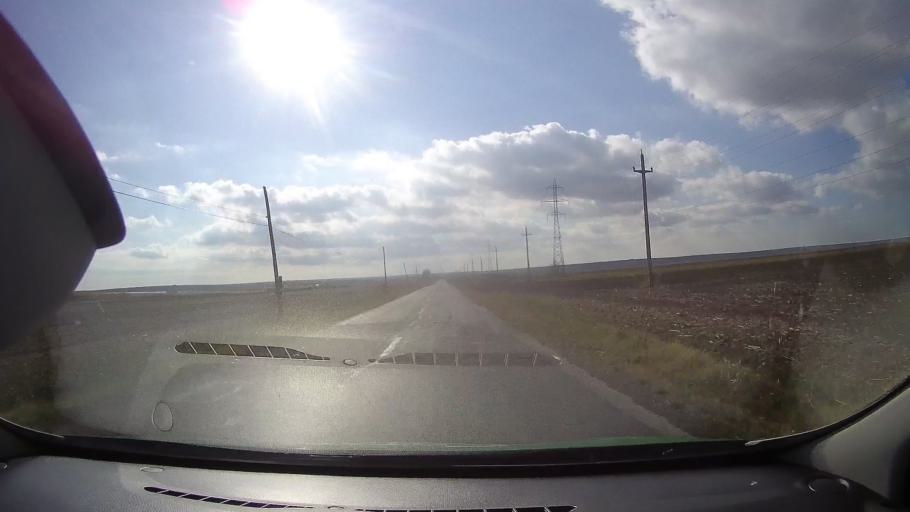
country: RO
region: Constanta
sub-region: Comuna Istria
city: Istria
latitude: 44.5405
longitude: 28.6894
